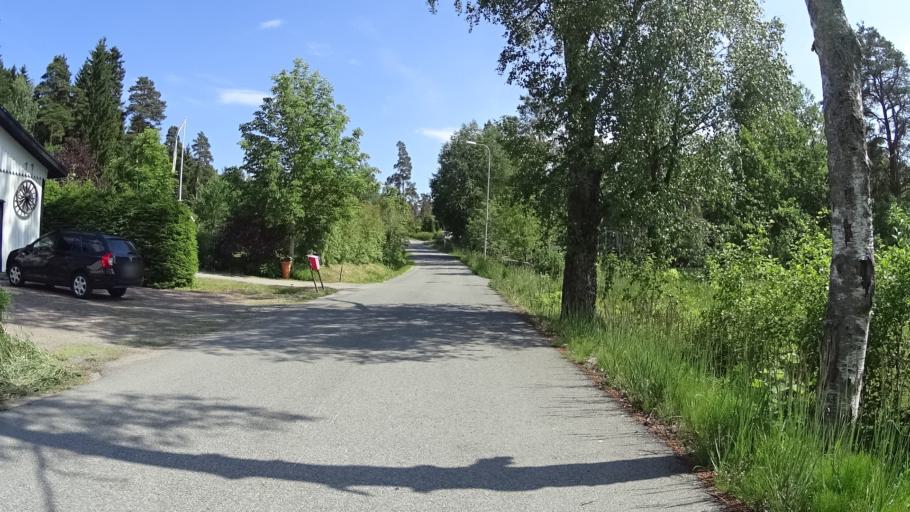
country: FI
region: Uusimaa
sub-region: Raaseporin
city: Karis
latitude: 60.0868
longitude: 23.6507
